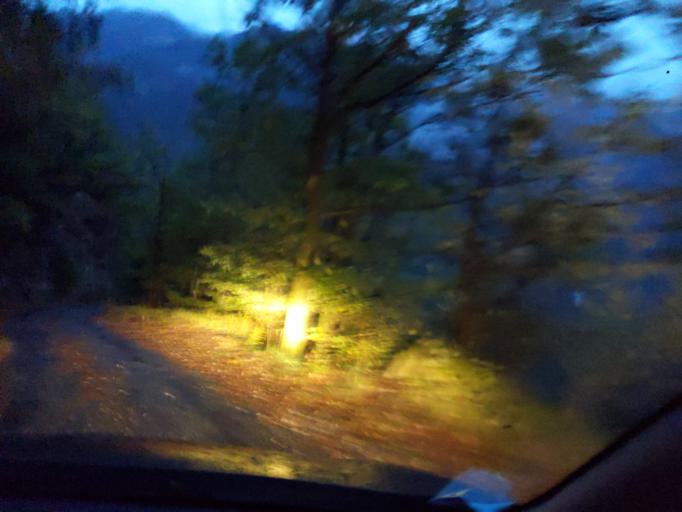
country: FR
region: Rhone-Alpes
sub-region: Departement de la Savoie
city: Aiton
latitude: 45.5199
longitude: 6.3260
